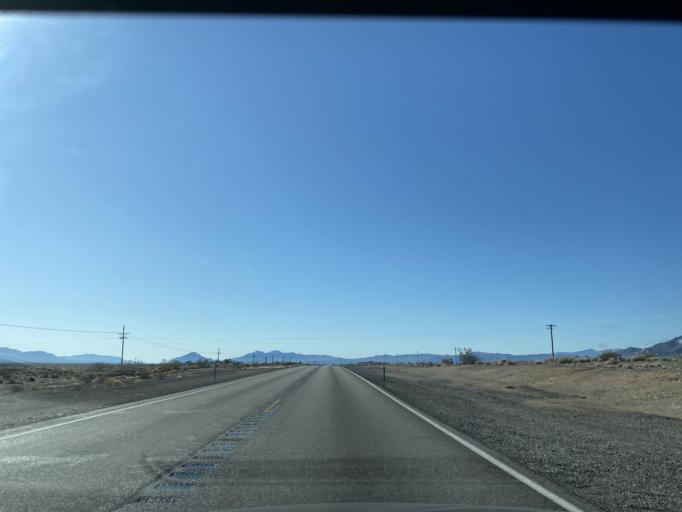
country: US
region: Nevada
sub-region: Nye County
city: Pahrump
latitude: 36.4270
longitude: -116.4221
